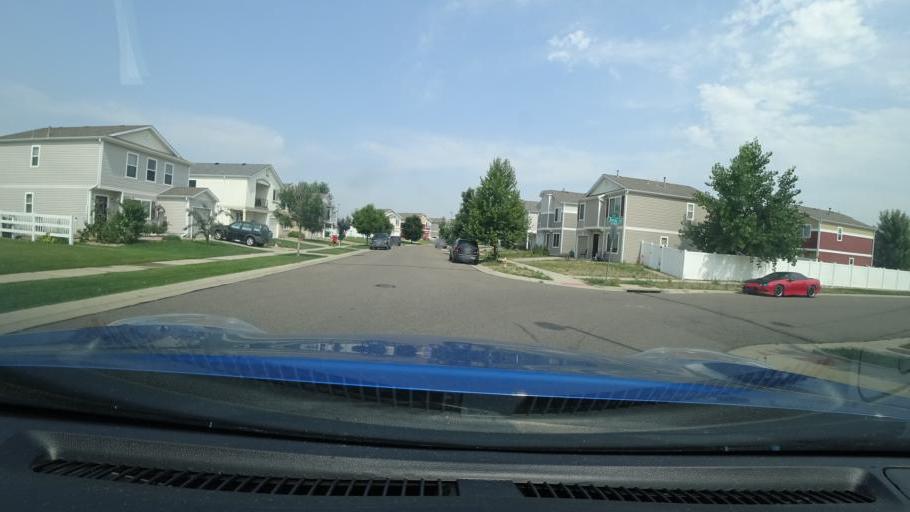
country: US
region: Colorado
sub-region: Adams County
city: Aurora
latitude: 39.7784
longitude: -104.7709
